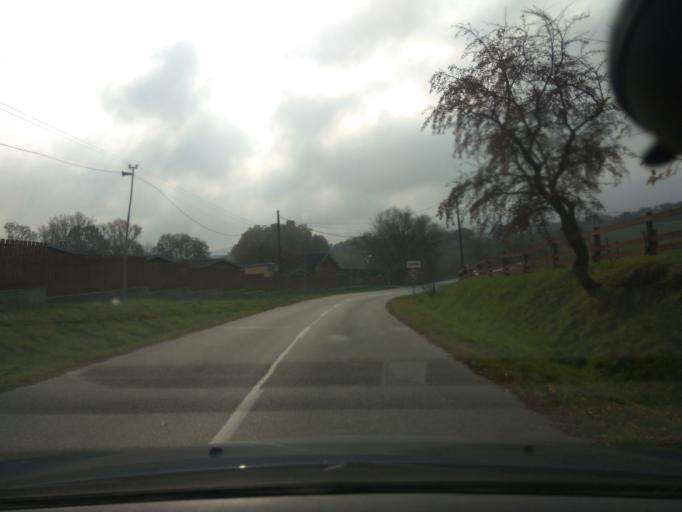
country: SK
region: Trnavsky
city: Vrbove
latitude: 48.6789
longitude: 17.6683
